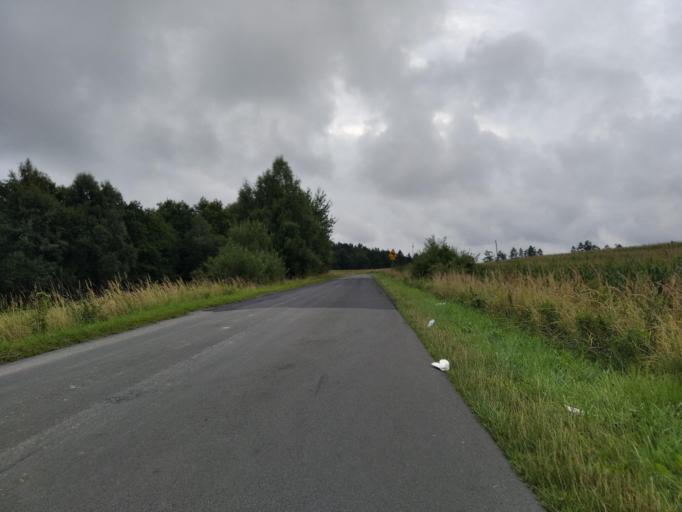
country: PL
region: Subcarpathian Voivodeship
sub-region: Powiat rzeszowski
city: Dynow
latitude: 49.7245
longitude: 22.3097
